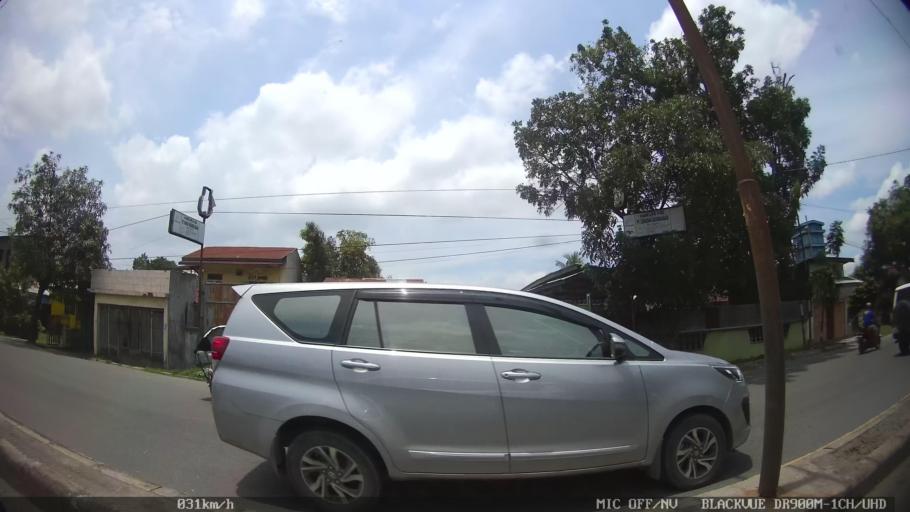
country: ID
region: North Sumatra
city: Labuhan Deli
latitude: 3.7101
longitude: 98.6796
